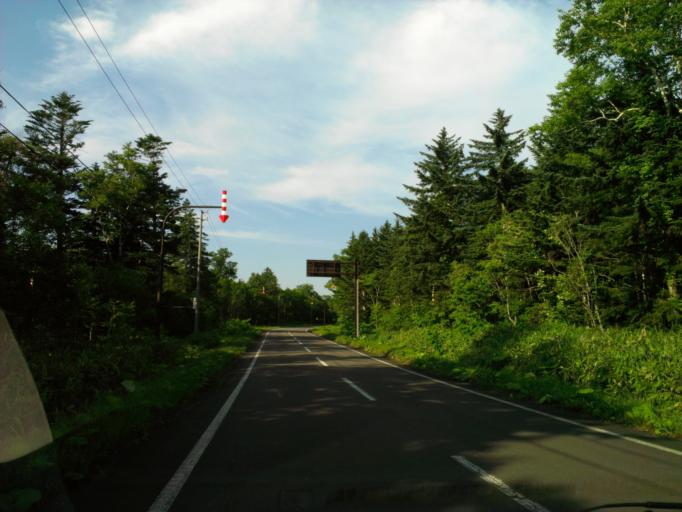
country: JP
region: Hokkaido
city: Shimo-furano
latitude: 43.4930
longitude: 142.6536
